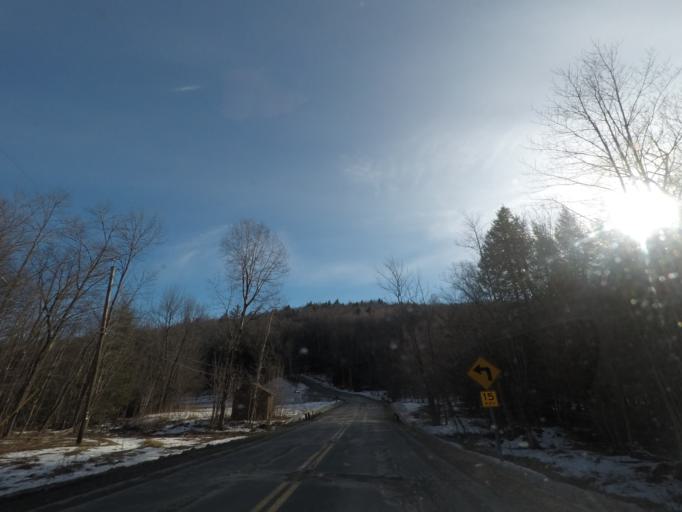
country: US
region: New York
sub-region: Rensselaer County
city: Hoosick Falls
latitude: 42.7371
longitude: -73.3807
